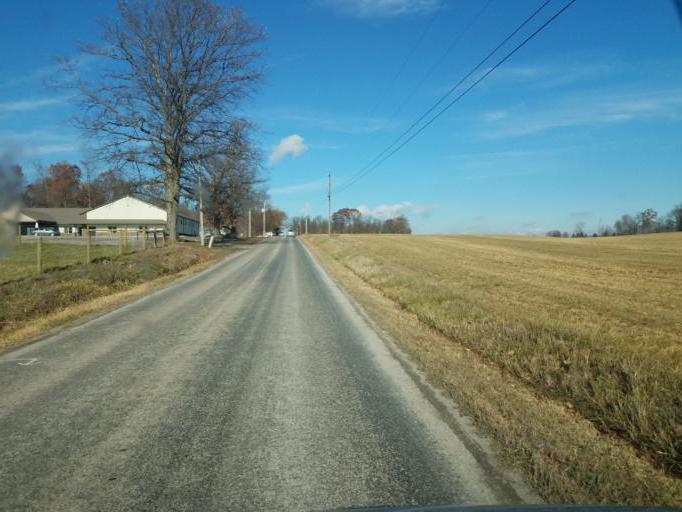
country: US
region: Ohio
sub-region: Wayne County
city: Apple Creek
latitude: 40.7445
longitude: -81.7752
